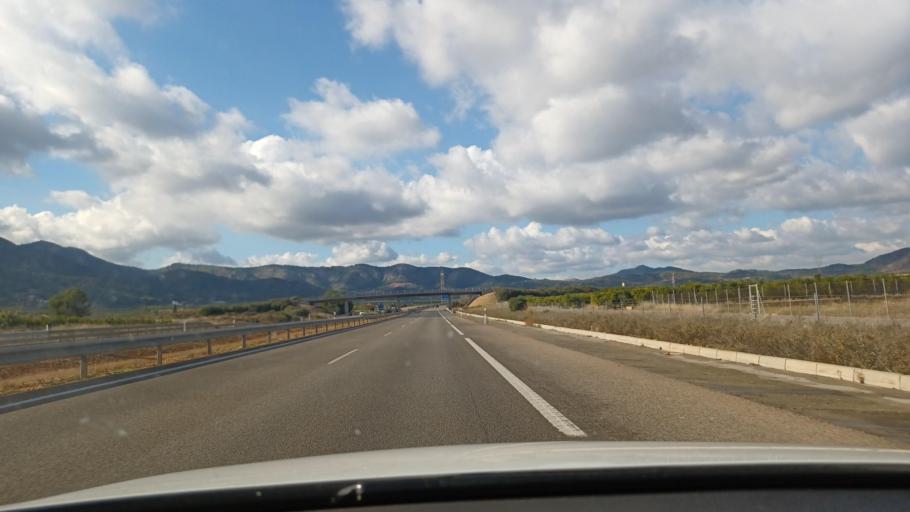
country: ES
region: Valencia
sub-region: Provincia de Castello
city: Villavieja
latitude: 39.8676
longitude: -0.1776
